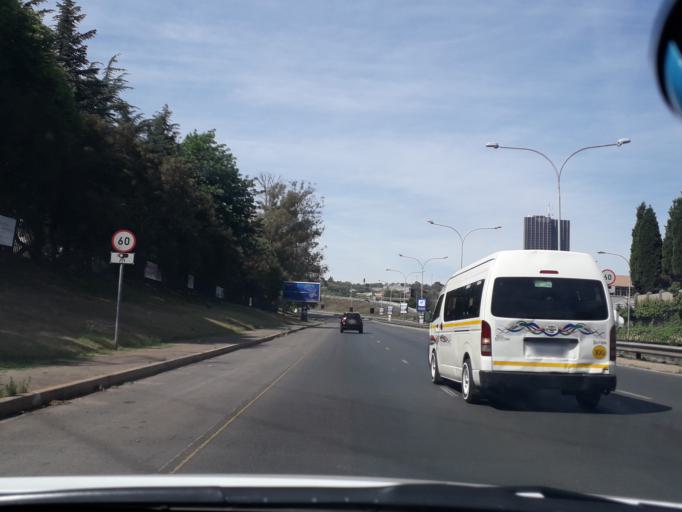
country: ZA
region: Gauteng
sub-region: City of Johannesburg Metropolitan Municipality
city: Johannesburg
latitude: -26.1773
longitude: 28.0171
